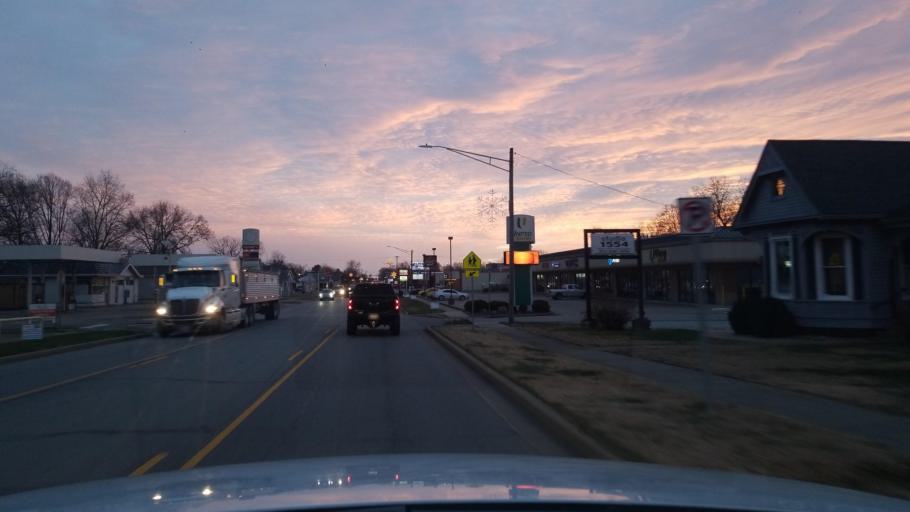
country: US
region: Indiana
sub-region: Posey County
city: Mount Vernon
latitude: 37.9332
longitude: -87.8914
